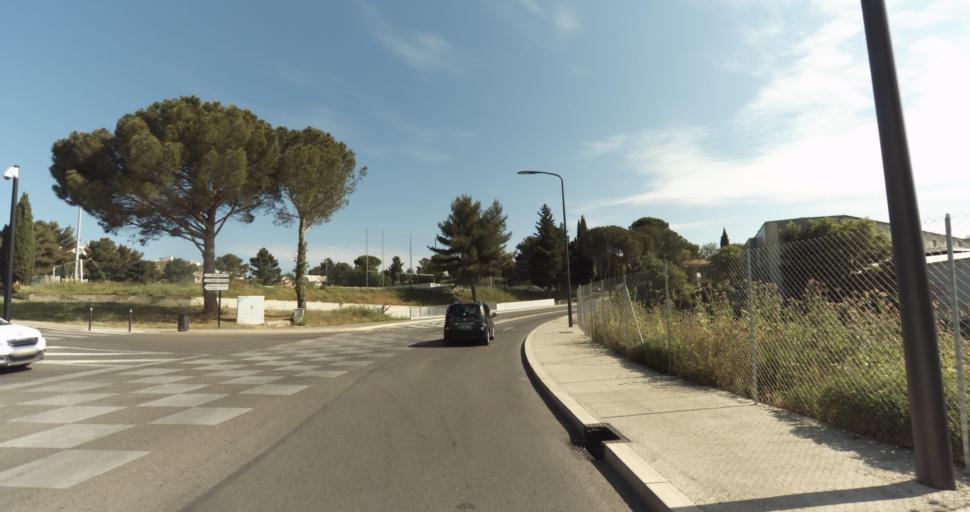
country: FR
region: Languedoc-Roussillon
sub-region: Departement du Gard
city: Nimes
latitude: 43.8288
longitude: 4.3334
